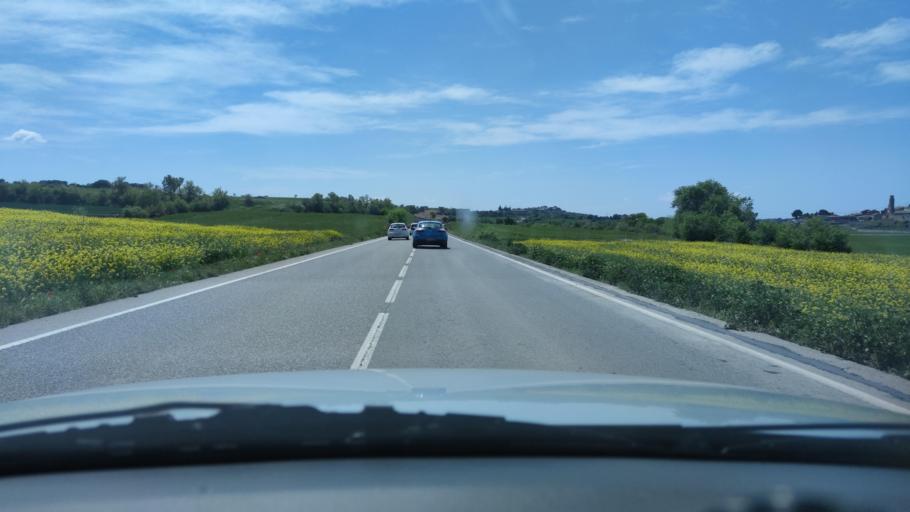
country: ES
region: Catalonia
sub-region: Provincia de Lleida
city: Mont-roig del Camp
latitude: 41.7761
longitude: 1.2660
